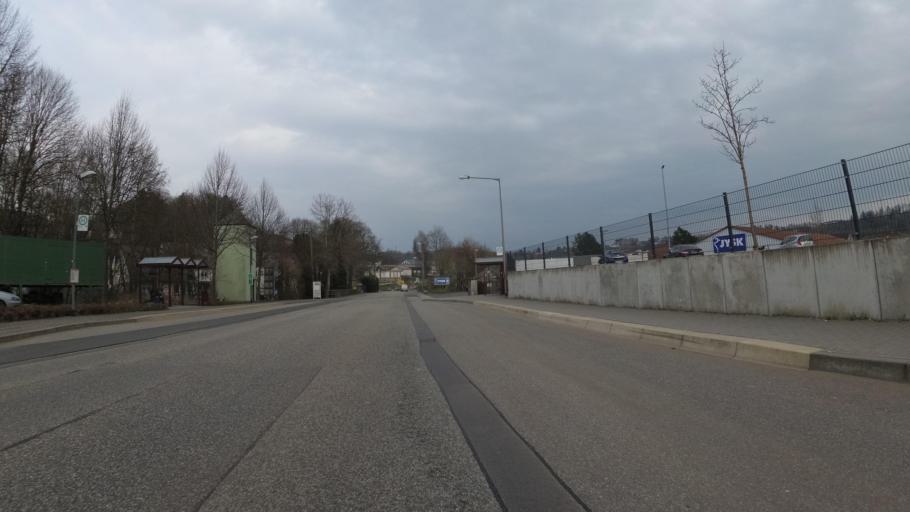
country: DE
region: Rheinland-Pfalz
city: Birkenfeld
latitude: 49.6484
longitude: 7.1599
